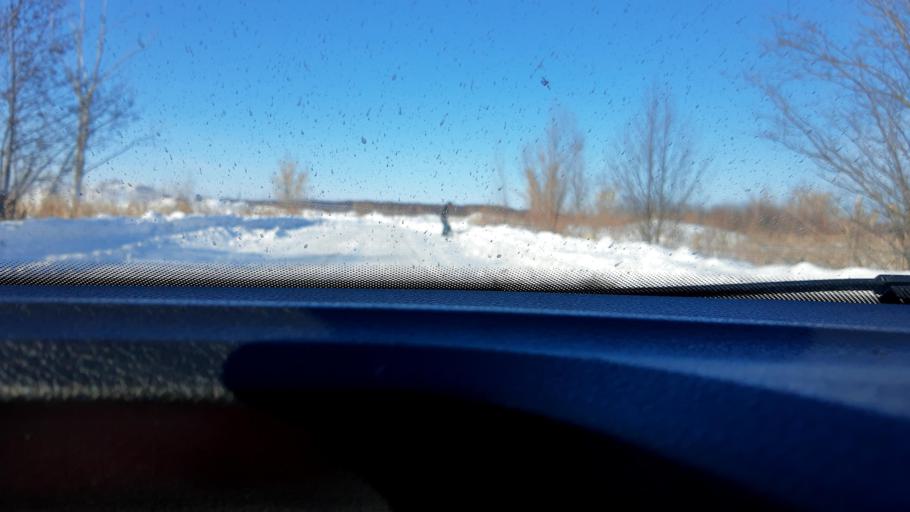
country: RU
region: Bashkortostan
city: Mikhaylovka
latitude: 54.7170
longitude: 55.8361
